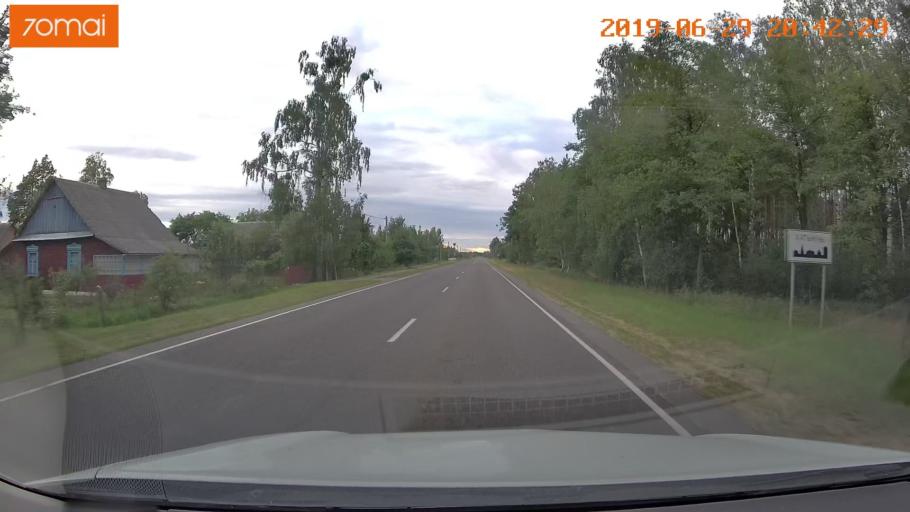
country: BY
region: Brest
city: Hantsavichy
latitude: 52.5981
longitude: 26.3252
